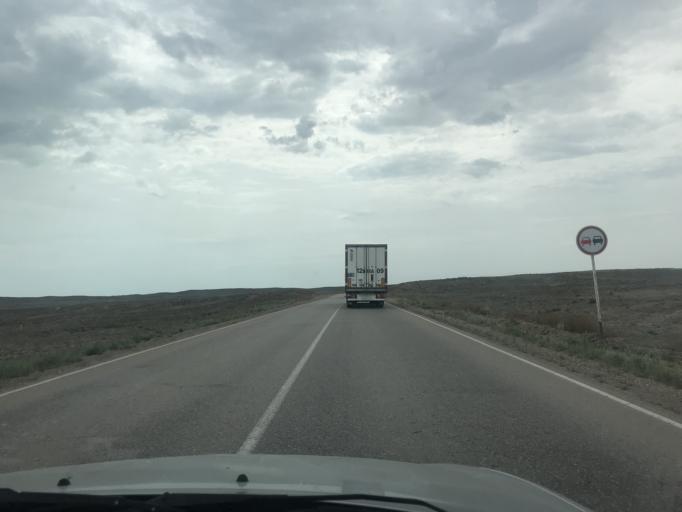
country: KZ
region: Zhambyl
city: Mynaral
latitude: 45.4993
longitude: 73.5165
